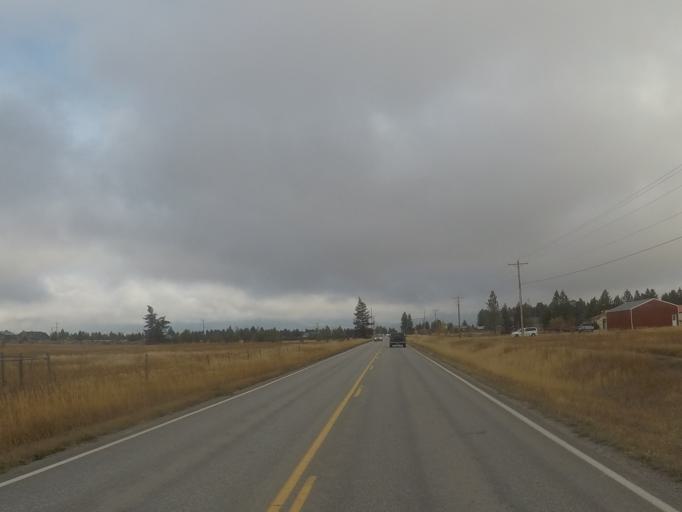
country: US
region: Montana
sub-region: Flathead County
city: Columbia Falls
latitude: 48.3470
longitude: -114.1593
